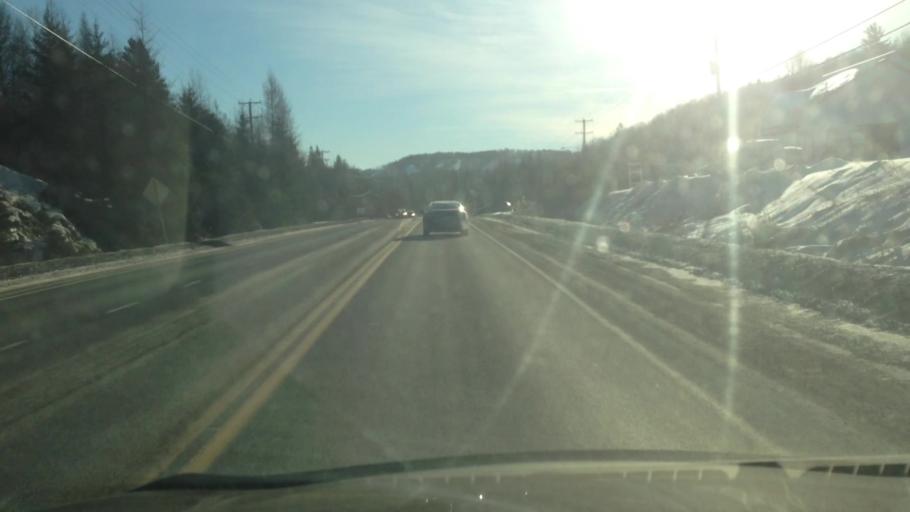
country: CA
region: Quebec
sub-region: Laurentides
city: Saint-Sauveur
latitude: 45.8901
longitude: -74.1922
